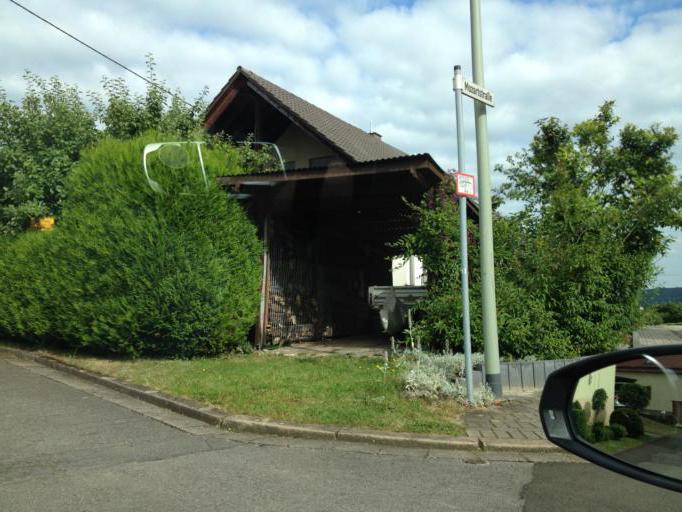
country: DE
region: Saarland
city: Tholey
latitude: 49.5001
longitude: 7.0328
